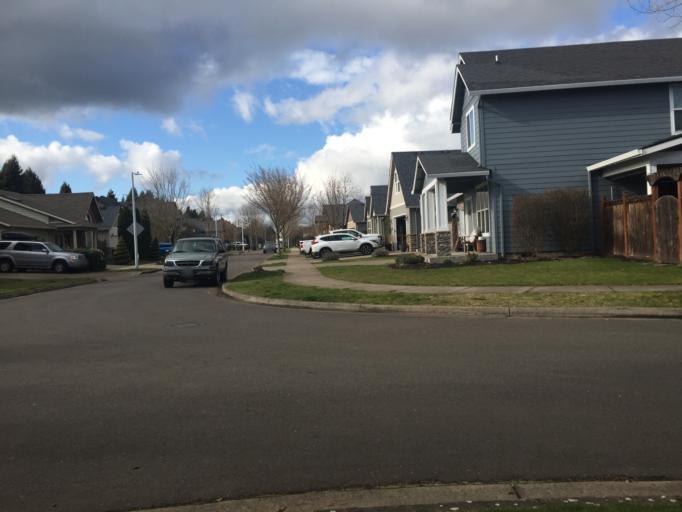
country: US
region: Oregon
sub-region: Lane County
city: Eugene
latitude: 44.0995
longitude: -123.1555
